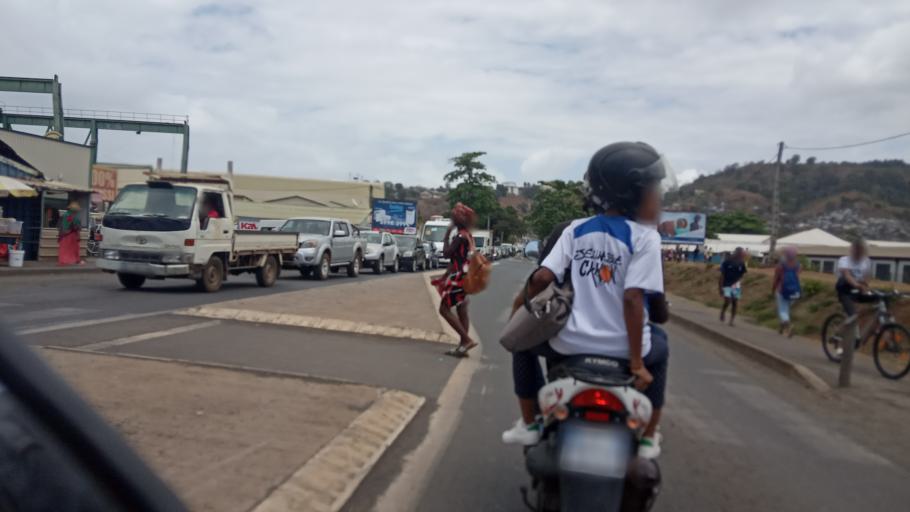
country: YT
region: Mamoudzou
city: Mamoudzou
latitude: -12.7674
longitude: 45.2246
